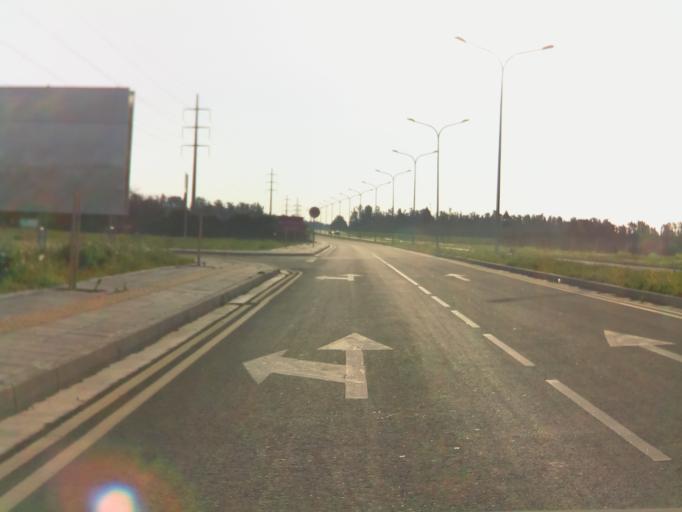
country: CY
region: Pafos
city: Paphos
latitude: 34.7395
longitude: 32.4527
